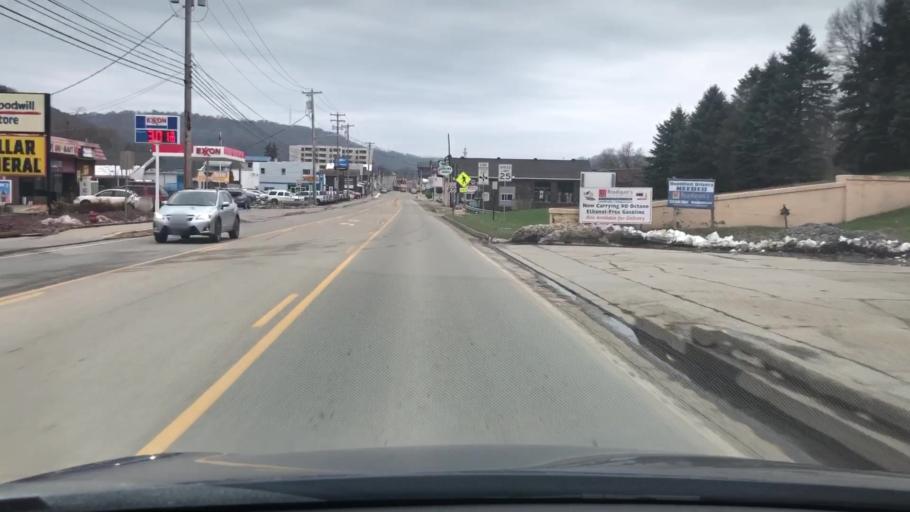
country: US
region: Pennsylvania
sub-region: Clarion County
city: Clarion
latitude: 41.0023
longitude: -79.3265
